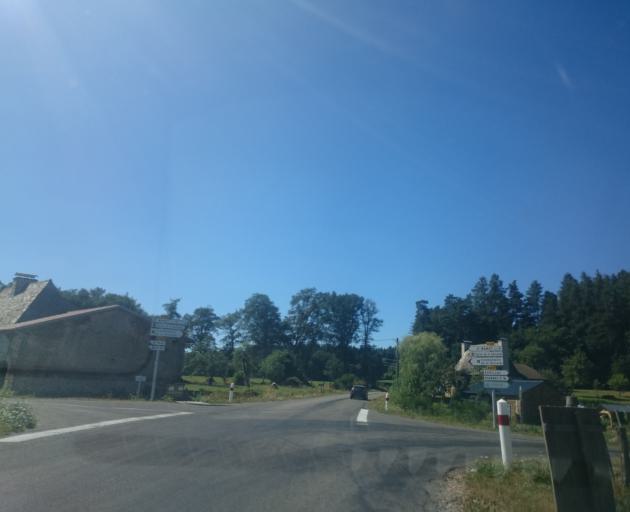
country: FR
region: Auvergne
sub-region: Departement du Cantal
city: Sansac-de-Marmiesse
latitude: 44.8221
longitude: 2.3645
